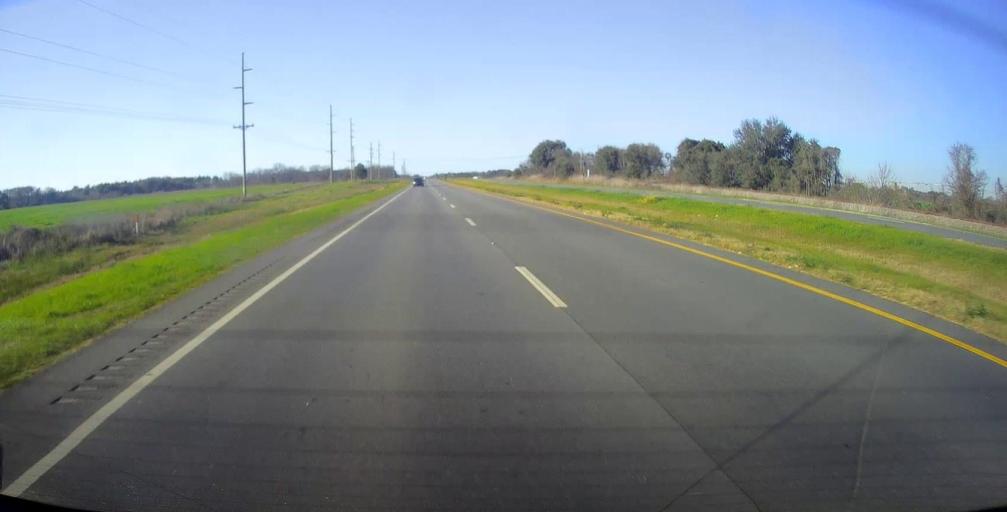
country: US
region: Georgia
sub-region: Lee County
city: Leesburg
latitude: 31.7768
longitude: -84.1934
